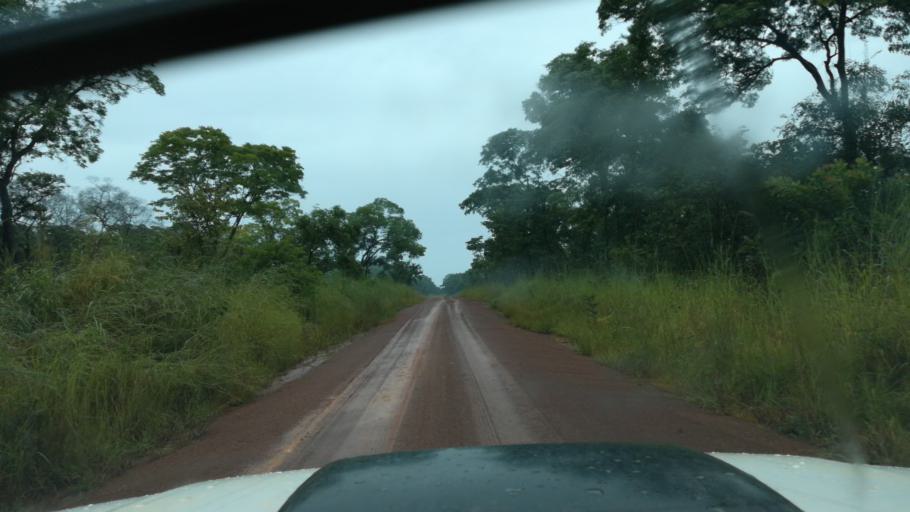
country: ZM
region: Luapula
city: Mwense
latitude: -10.3474
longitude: 28.1087
